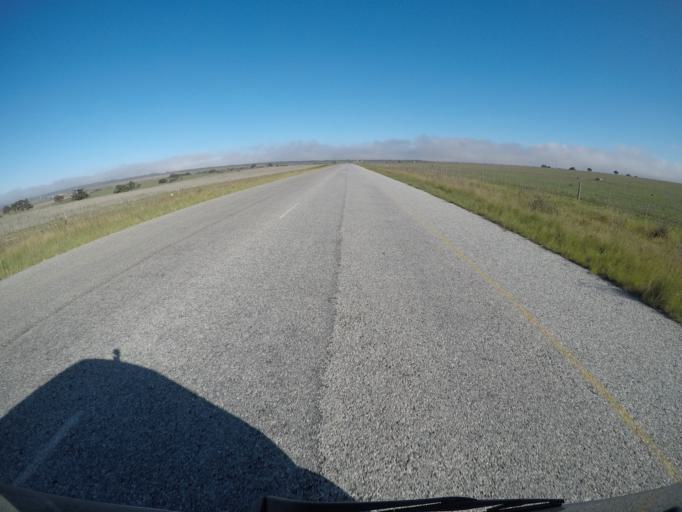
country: ZA
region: Western Cape
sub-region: Eden District Municipality
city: Mossel Bay
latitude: -34.1761
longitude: 22.0160
